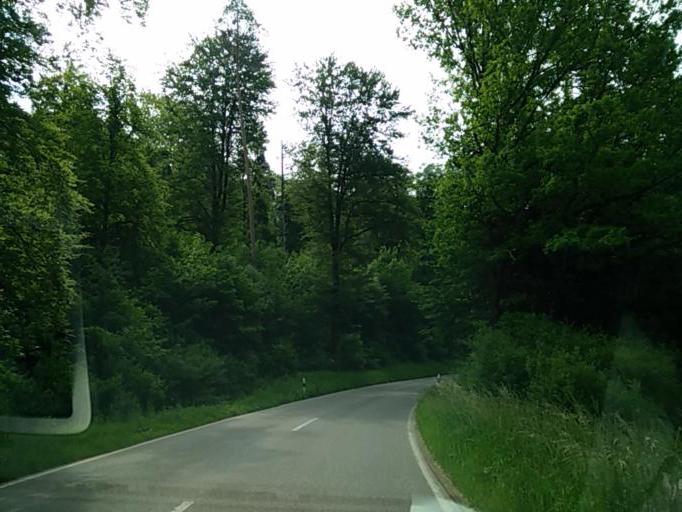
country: DE
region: Baden-Wuerttemberg
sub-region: Tuebingen Region
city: Hirrlingen
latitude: 48.4278
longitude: 8.8696
